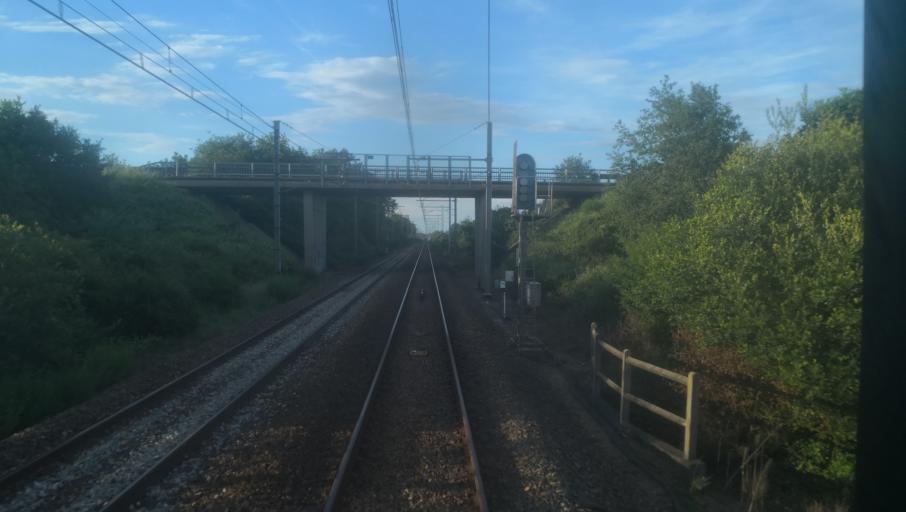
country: FR
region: Centre
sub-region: Departement de l'Indre
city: Luant
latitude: 46.6978
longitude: 1.5651
